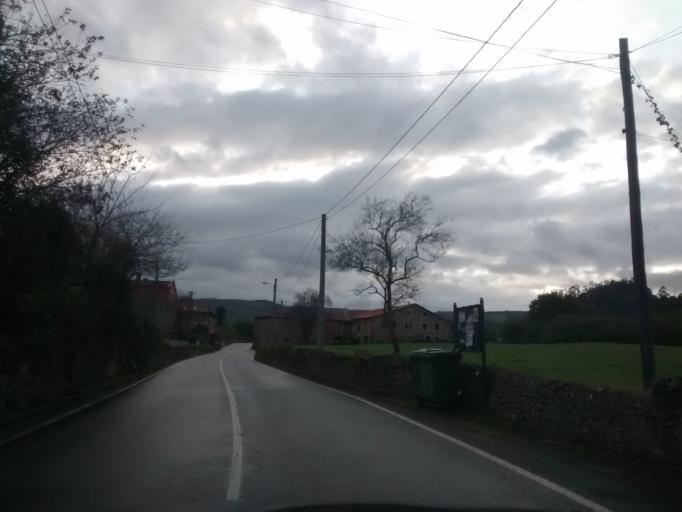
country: ES
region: Cantabria
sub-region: Provincia de Cantabria
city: Lierganes
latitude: 43.3497
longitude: -3.7293
